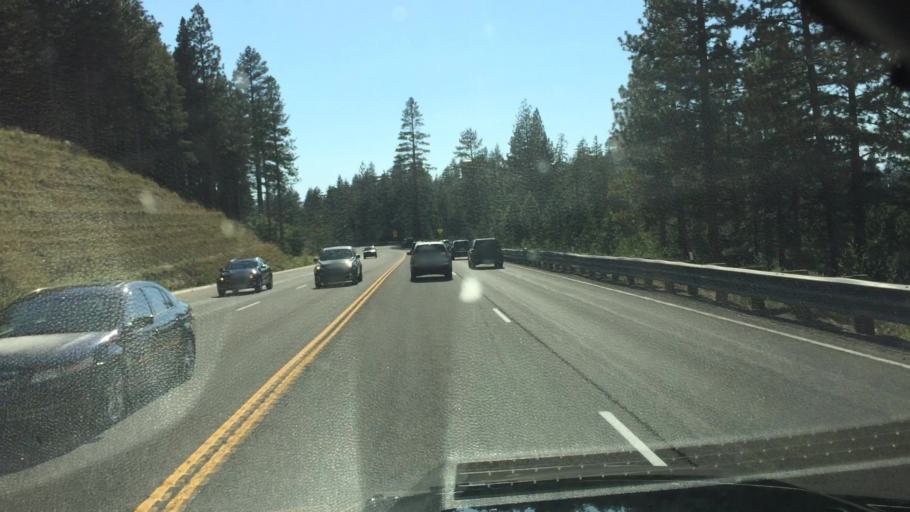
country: US
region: Nevada
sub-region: Douglas County
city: Kingsbury
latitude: 39.0825
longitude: -119.9384
